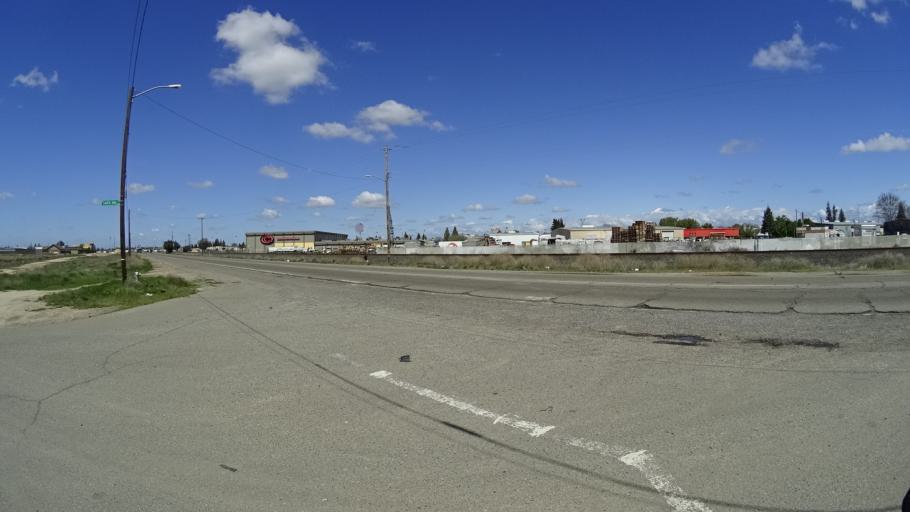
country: US
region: California
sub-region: Fresno County
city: West Park
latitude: 36.8045
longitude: -119.8738
